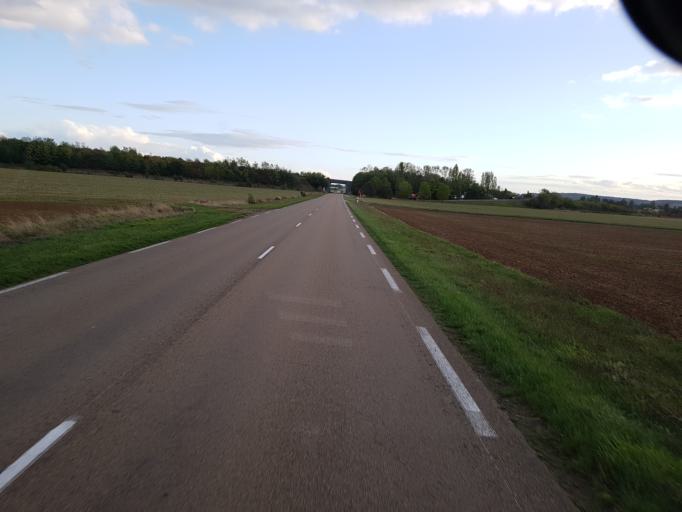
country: FR
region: Bourgogne
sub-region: Departement de l'Yonne
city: Soucy
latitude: 48.2602
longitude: 3.2830
